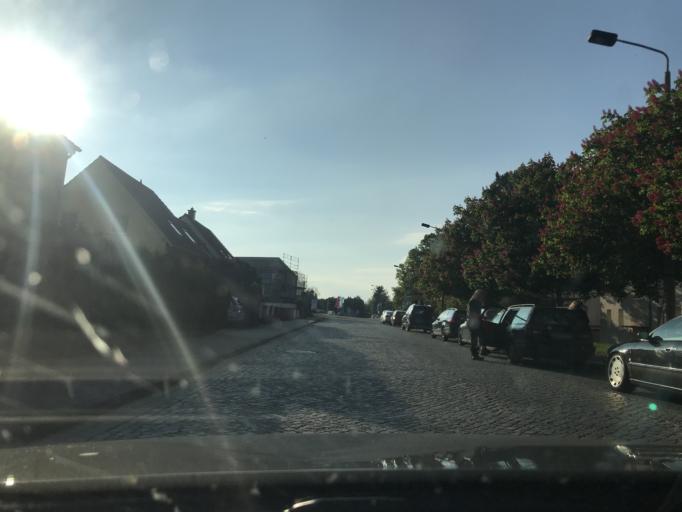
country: DE
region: Thuringia
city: Bad Langensalza
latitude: 51.1114
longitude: 10.6415
